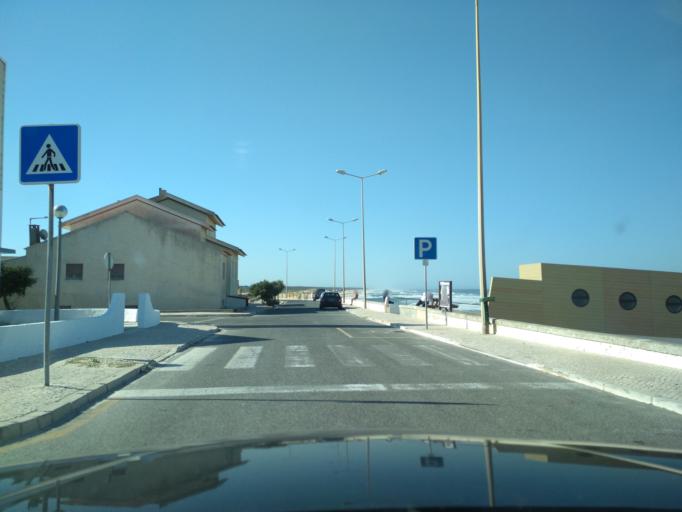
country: PT
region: Coimbra
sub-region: Figueira da Foz
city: Lavos
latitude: 40.0567
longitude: -8.8906
